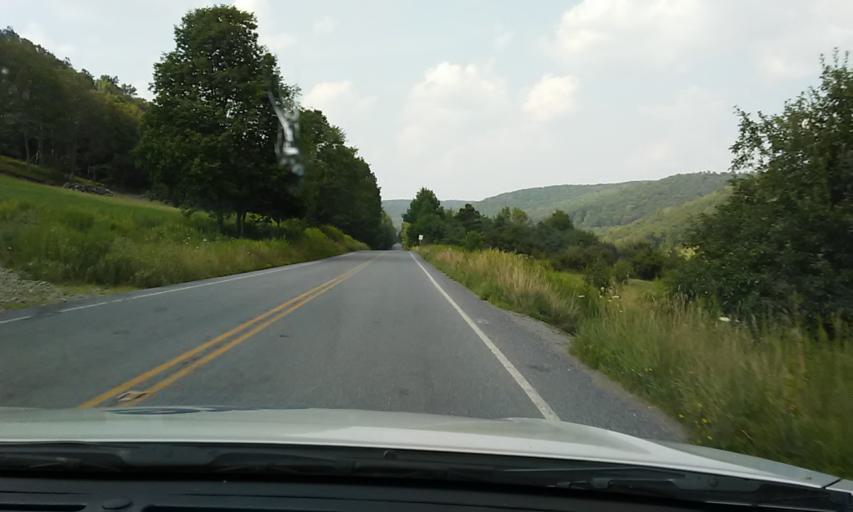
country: US
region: Pennsylvania
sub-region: Potter County
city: Coudersport
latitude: 41.8945
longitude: -77.8430
